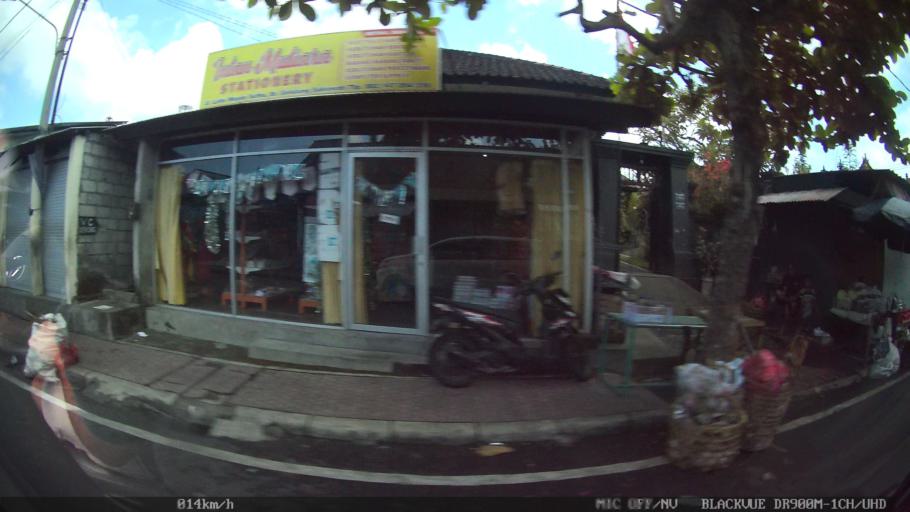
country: ID
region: Bali
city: Banjar Pasekan
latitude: -8.5940
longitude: 115.2803
